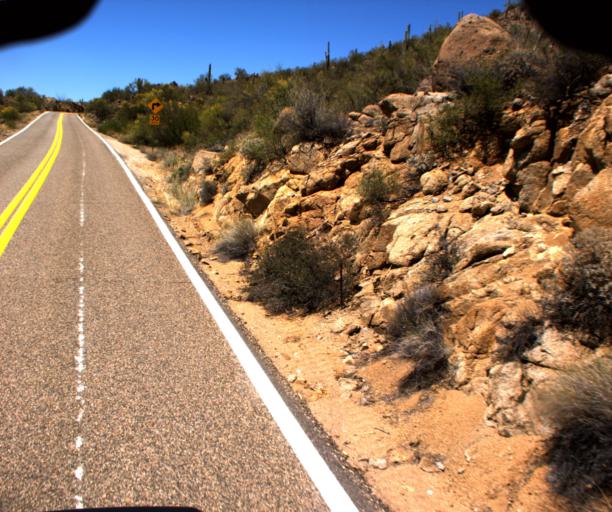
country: US
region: Arizona
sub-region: Yavapai County
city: Bagdad
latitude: 34.5090
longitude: -113.0759
